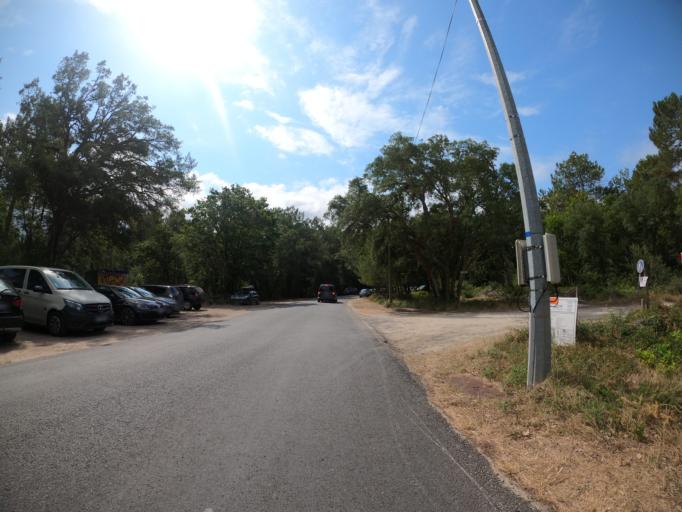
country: FR
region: Aquitaine
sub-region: Departement des Landes
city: Leon
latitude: 43.8888
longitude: -1.3677
